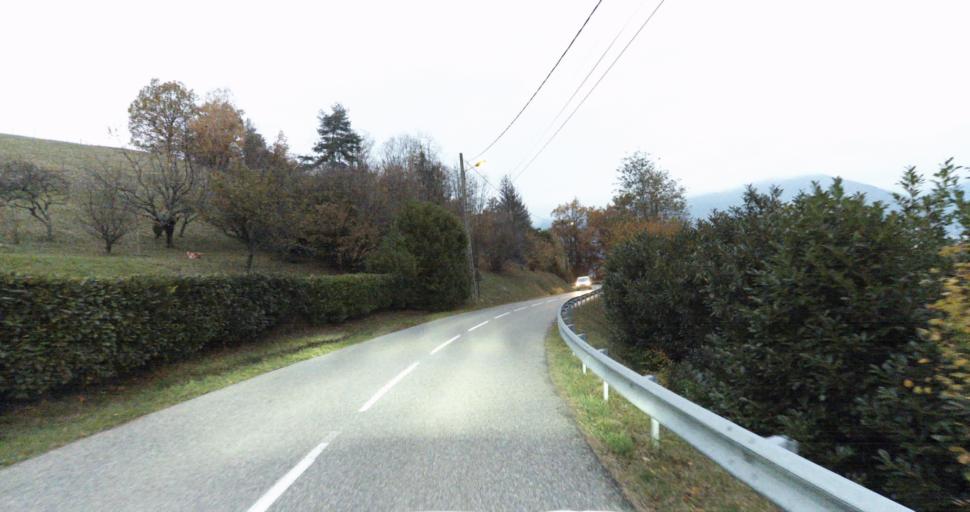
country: FR
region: Rhone-Alpes
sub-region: Departement de la Haute-Savoie
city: Sevrier
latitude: 45.8506
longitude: 6.1372
